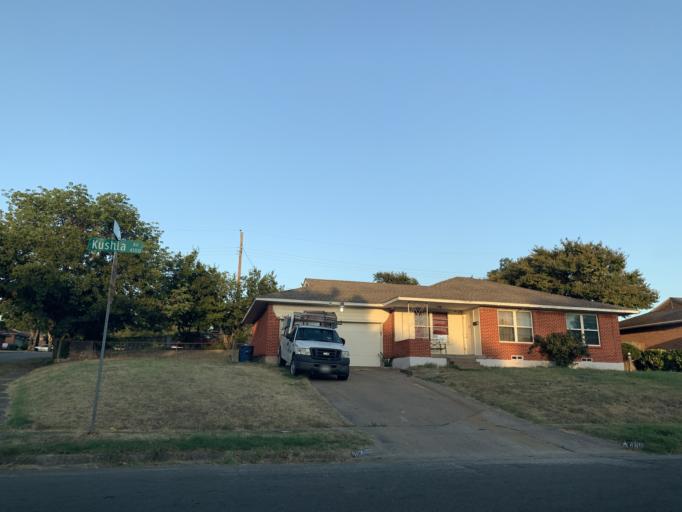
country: US
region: Texas
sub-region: Dallas County
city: Cockrell Hill
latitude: 32.6940
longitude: -96.8092
